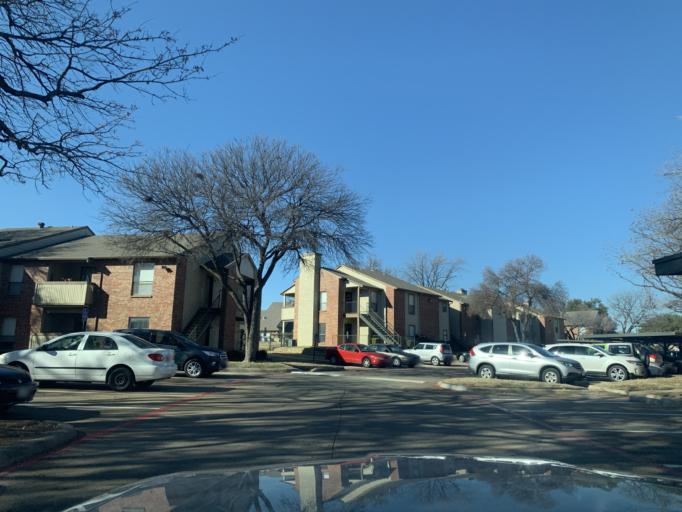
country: US
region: Texas
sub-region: Tarrant County
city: Bedford
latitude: 32.8409
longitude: -97.1453
